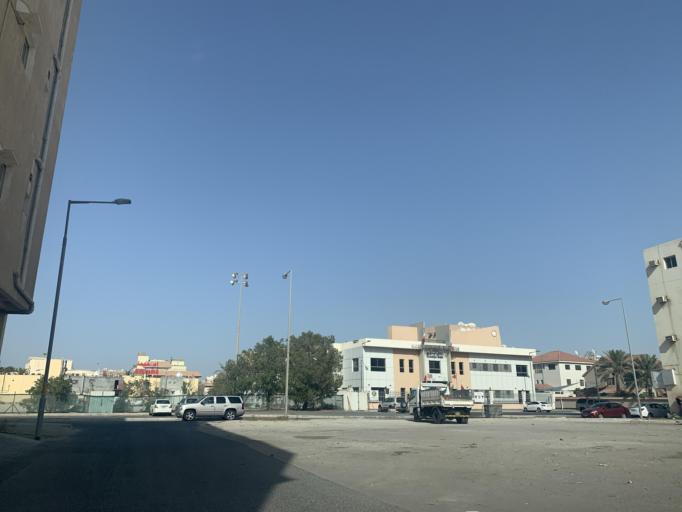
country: BH
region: Manama
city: Jidd Hafs
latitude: 26.2108
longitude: 50.4501
